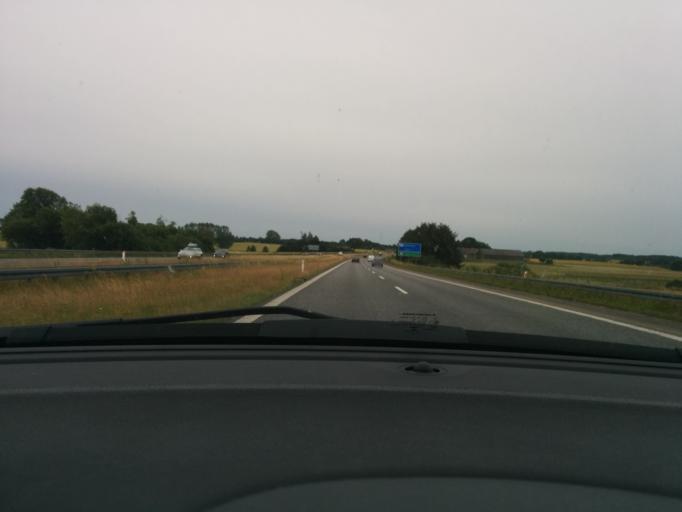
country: DK
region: Zealand
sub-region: Faxe Kommune
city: Ronnede
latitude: 55.2724
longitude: 12.0073
